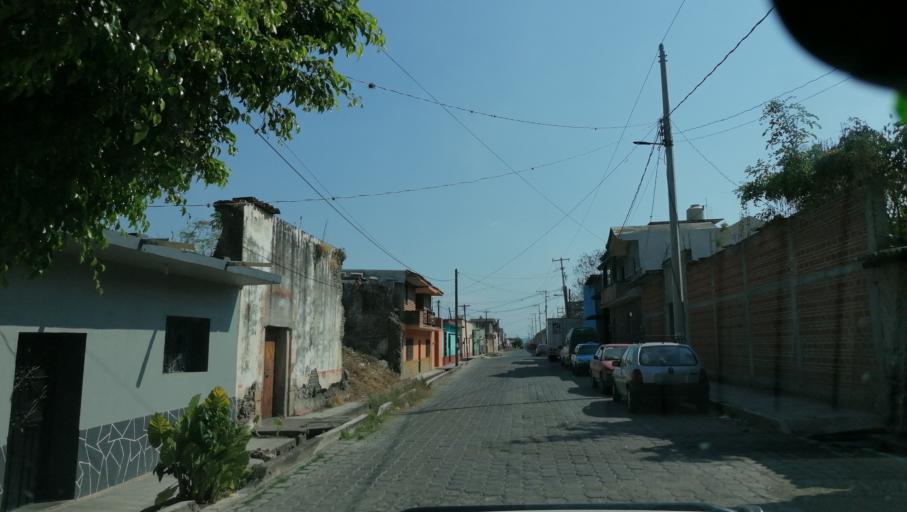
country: MX
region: Puebla
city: Huaquechula
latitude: 18.7711
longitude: -98.5394
